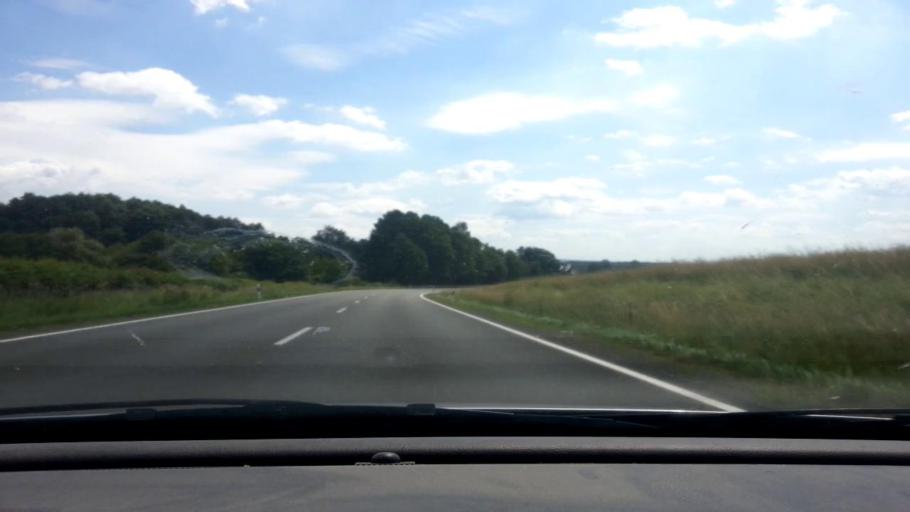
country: DE
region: Bavaria
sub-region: Upper Palatinate
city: Kemnath
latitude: 49.8676
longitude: 11.8577
